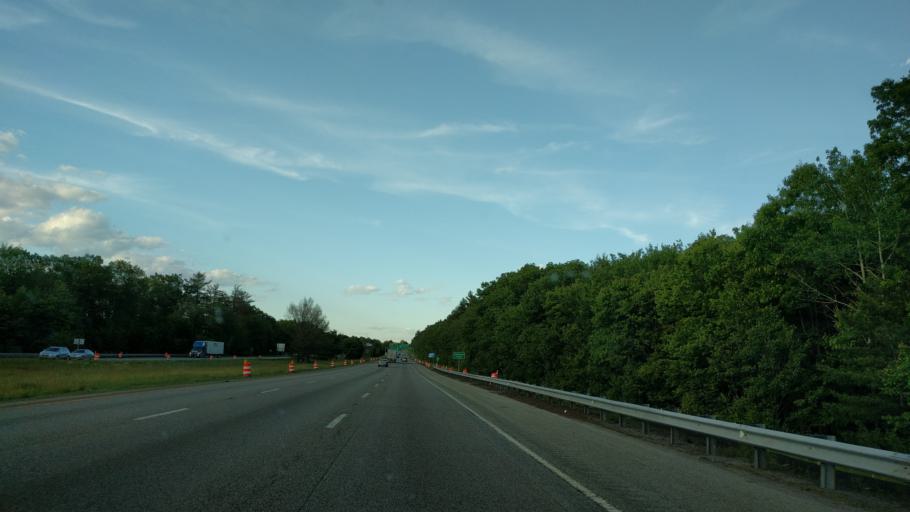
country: US
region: Massachusetts
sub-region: Worcester County
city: Berlin
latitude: 42.3516
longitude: -71.6151
